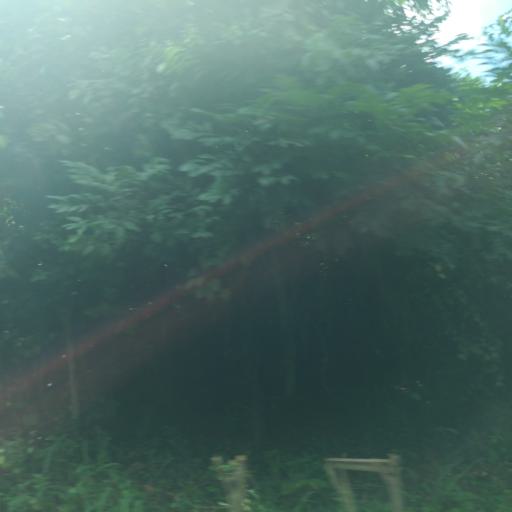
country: NG
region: Lagos
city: Ikorodu
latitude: 6.6723
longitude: 3.6471
